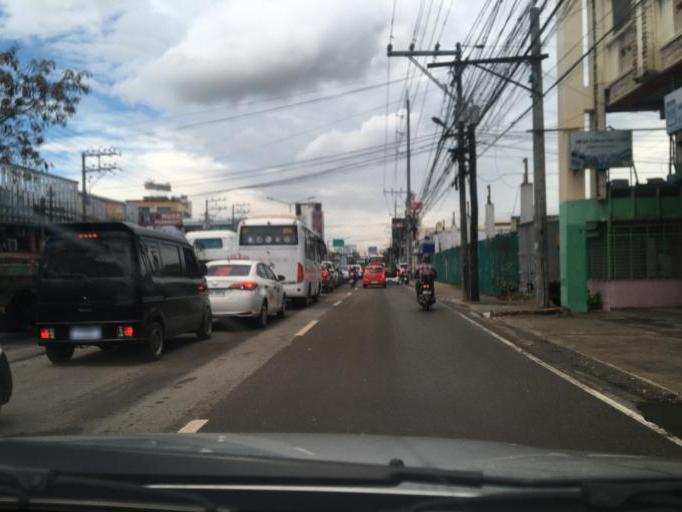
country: PH
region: Central Visayas
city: Mandaue City
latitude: 10.3331
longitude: 123.9368
